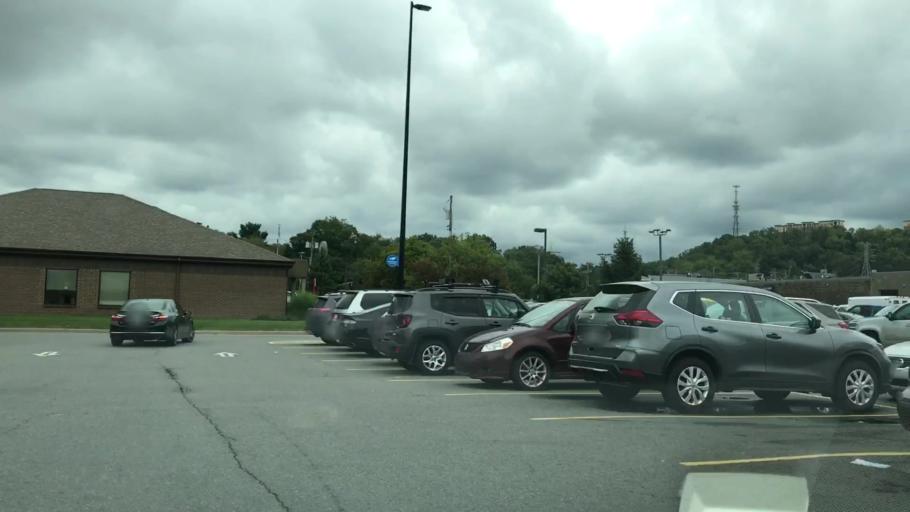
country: US
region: Pennsylvania
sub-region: Allegheny County
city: Heidelberg
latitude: 40.3868
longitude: -80.0948
